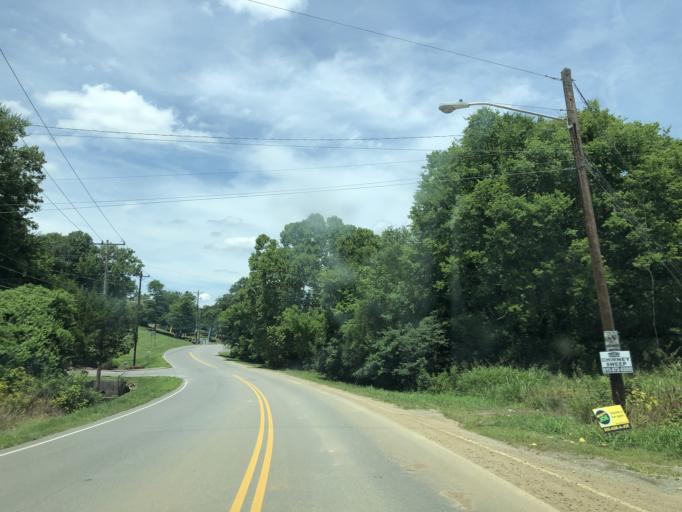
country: US
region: Tennessee
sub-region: Rutherford County
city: La Vergne
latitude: 36.0386
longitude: -86.6585
